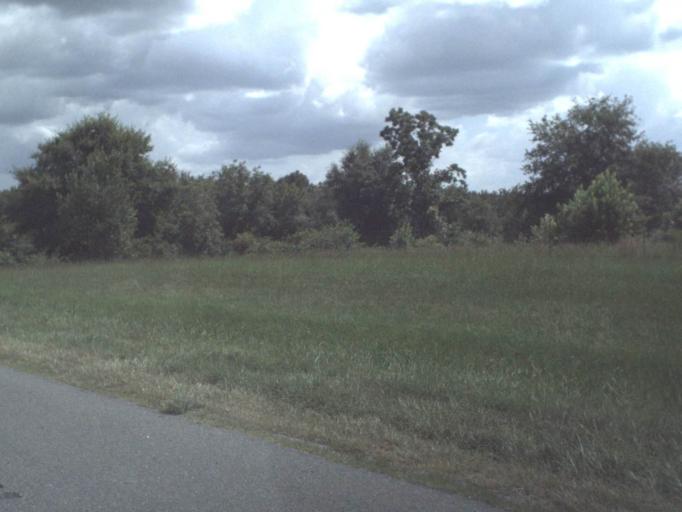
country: US
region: Florida
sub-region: Columbia County
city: Lake City
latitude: 30.0510
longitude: -82.6220
